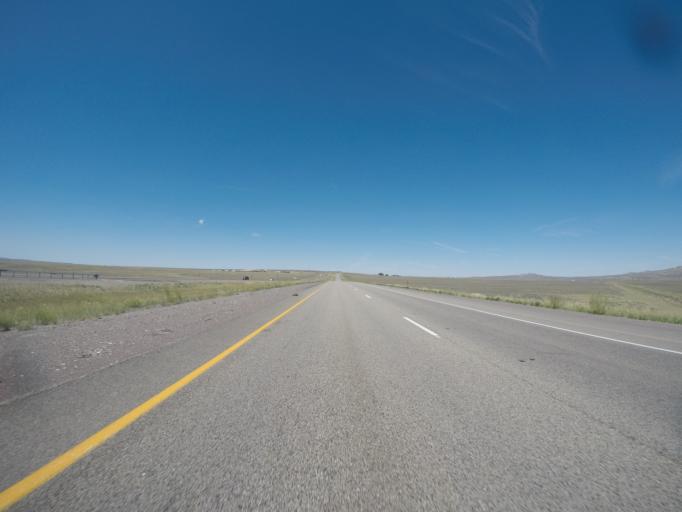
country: US
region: Wyoming
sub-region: Carbon County
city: Saratoga
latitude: 41.7420
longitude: -106.8073
